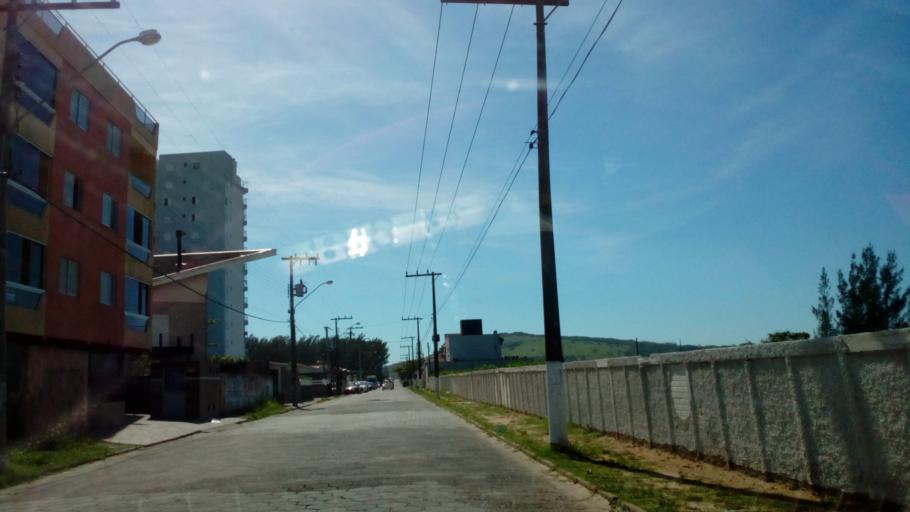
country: BR
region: Santa Catarina
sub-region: Laguna
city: Laguna
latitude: -28.4940
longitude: -48.7698
